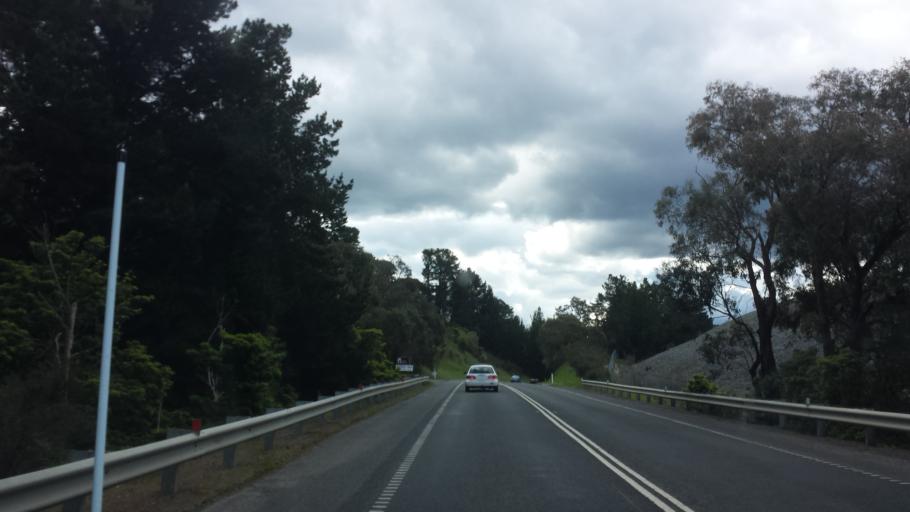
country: AU
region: Victoria
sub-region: Yarra Ranges
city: Selby
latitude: -37.9502
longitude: 145.3846
